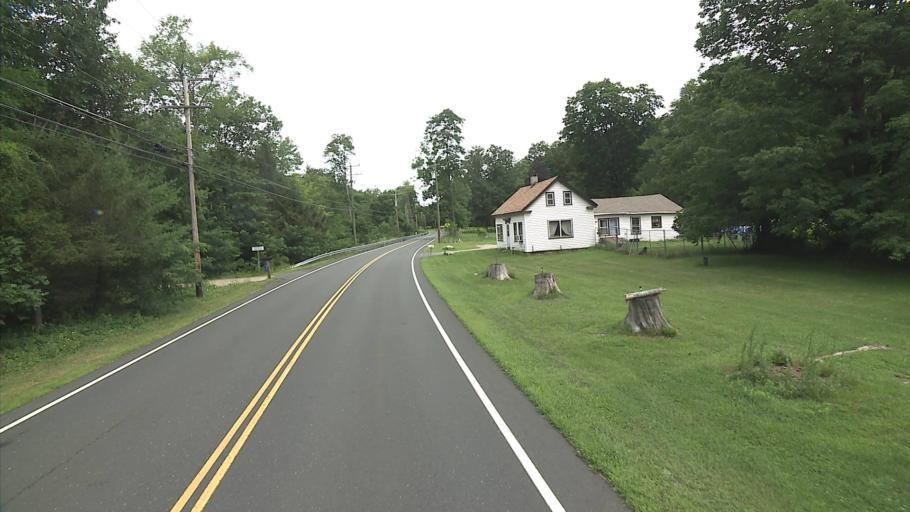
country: US
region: Connecticut
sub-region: Litchfield County
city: Winsted
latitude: 41.9831
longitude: -73.0453
